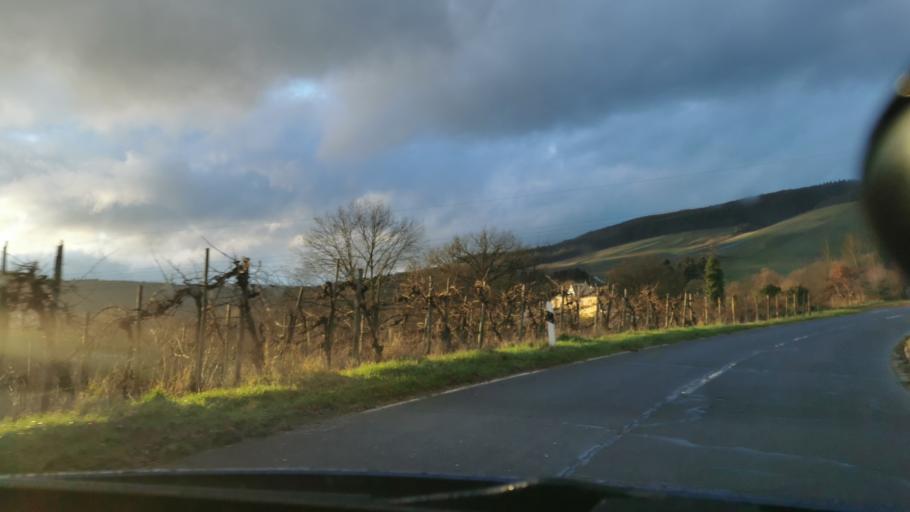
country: DE
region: Rheinland-Pfalz
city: Maring-Noviand
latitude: 49.9327
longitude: 6.9973
